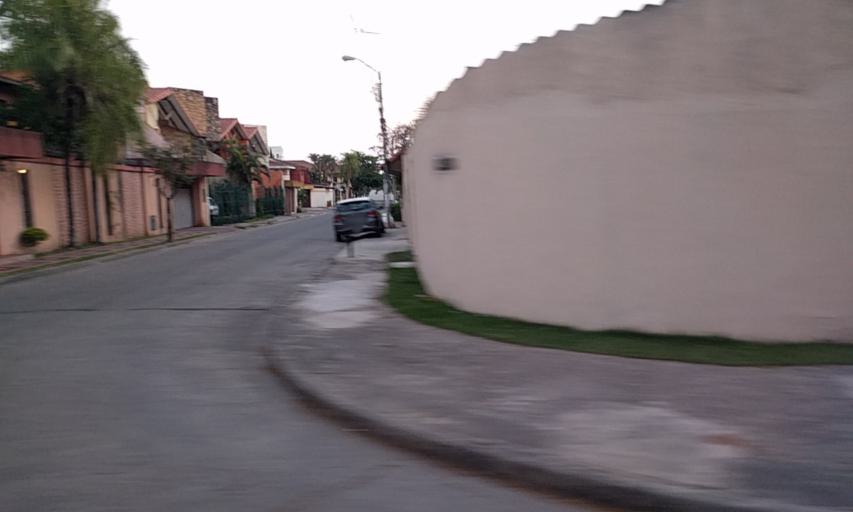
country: BO
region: Santa Cruz
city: Santa Cruz de la Sierra
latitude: -17.7667
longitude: -63.1684
